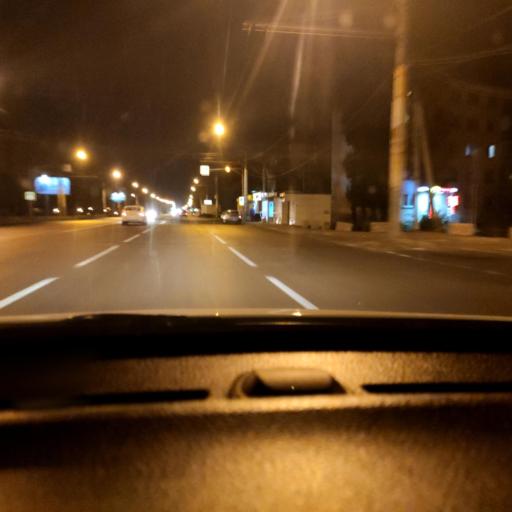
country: RU
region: Voronezj
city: Maslovka
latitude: 51.6041
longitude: 39.2371
